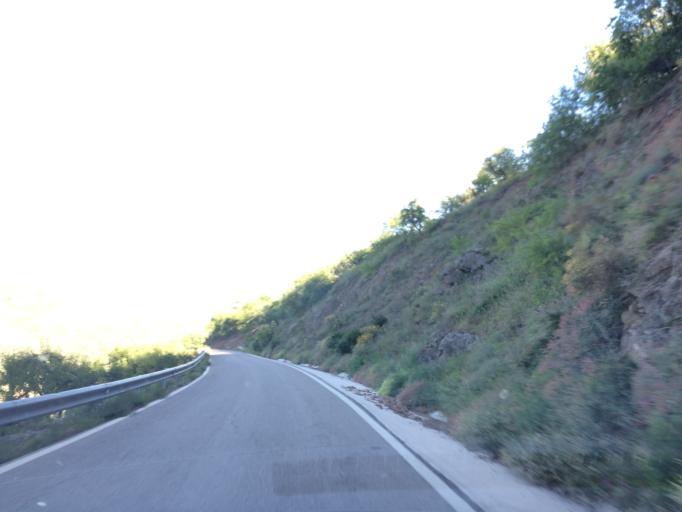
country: ES
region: Andalusia
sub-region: Provincia de Malaga
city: Totalan
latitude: 36.7800
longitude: -4.3191
